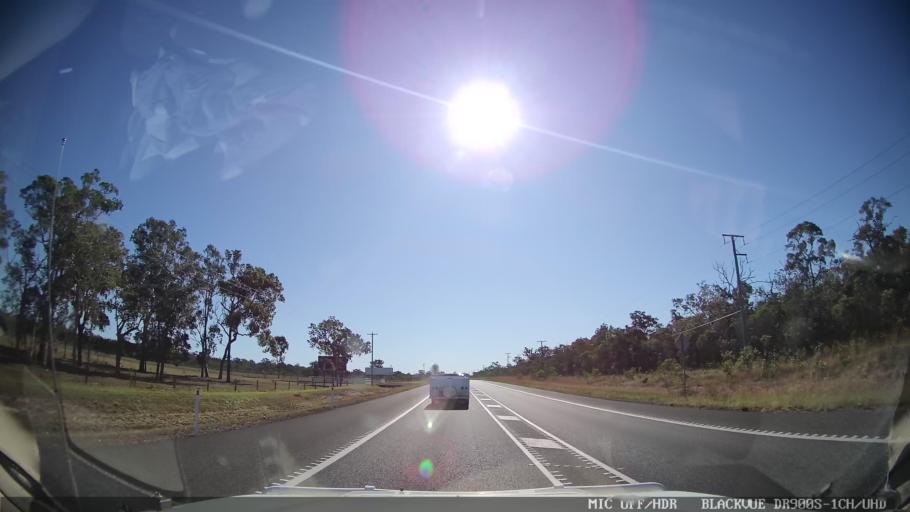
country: AU
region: Queensland
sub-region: Bundaberg
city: Childers
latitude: -25.2791
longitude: 152.3861
